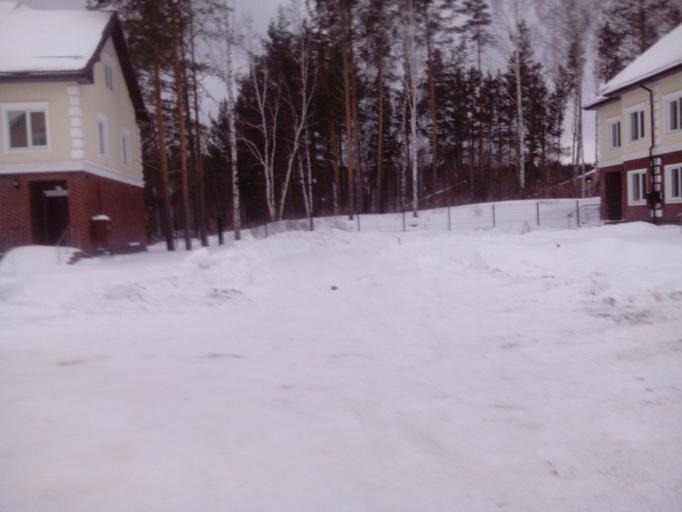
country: RU
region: Sverdlovsk
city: Shirokaya Rechka
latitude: 56.8073
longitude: 60.4764
